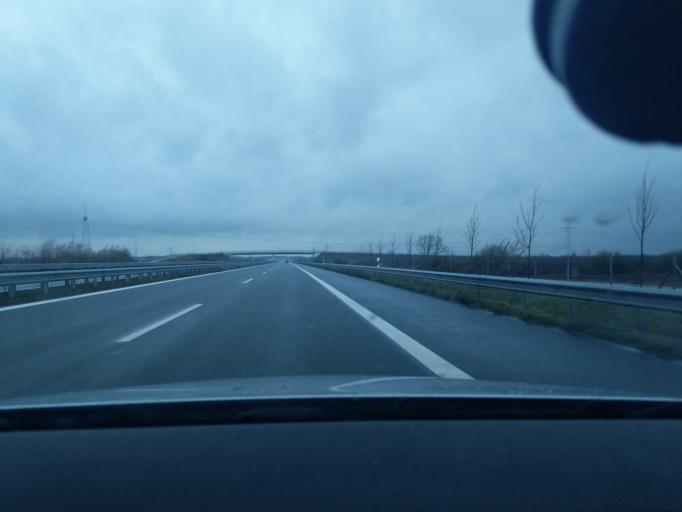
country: DE
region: Lower Saxony
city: Mittelnkirchen
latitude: 53.5086
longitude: 9.6369
